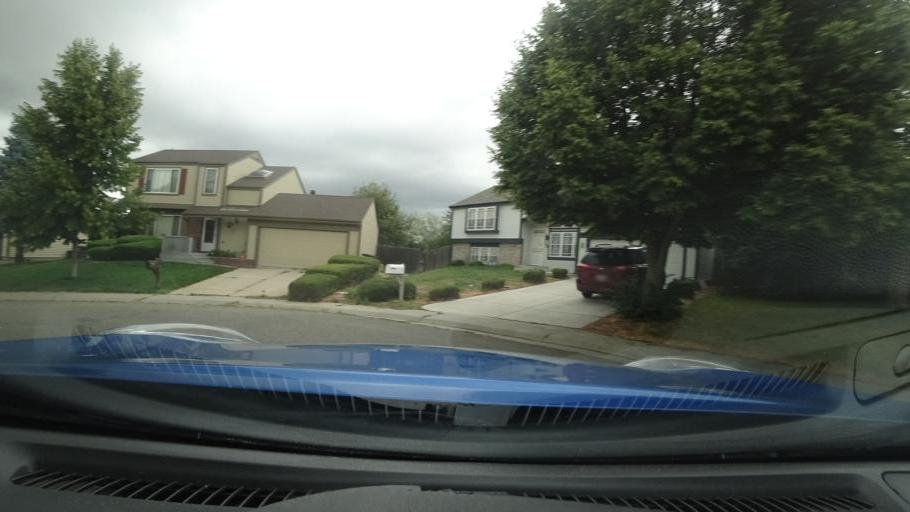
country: US
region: Colorado
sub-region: Adams County
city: Aurora
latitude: 39.7017
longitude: -104.8107
